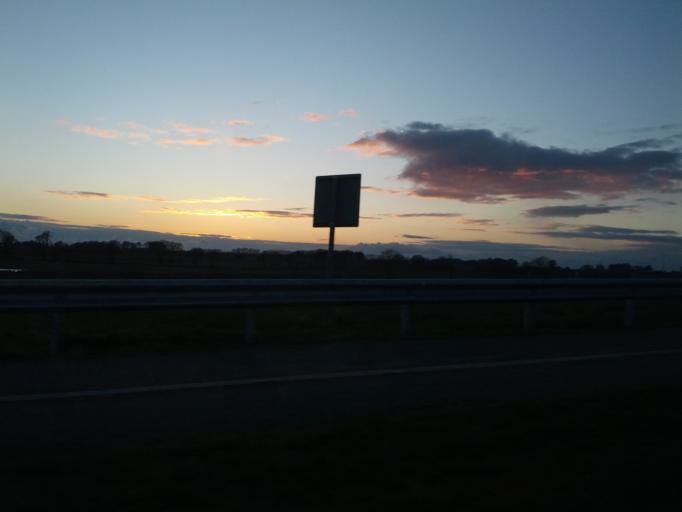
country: IE
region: Connaught
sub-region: County Galway
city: Athenry
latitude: 53.2927
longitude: -8.7577
